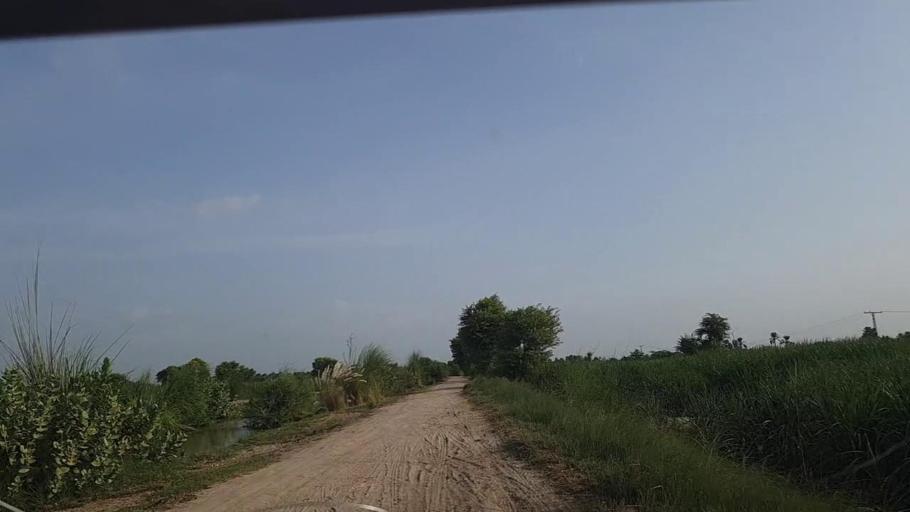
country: PK
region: Sindh
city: Ghotki
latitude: 27.9996
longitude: 69.2618
